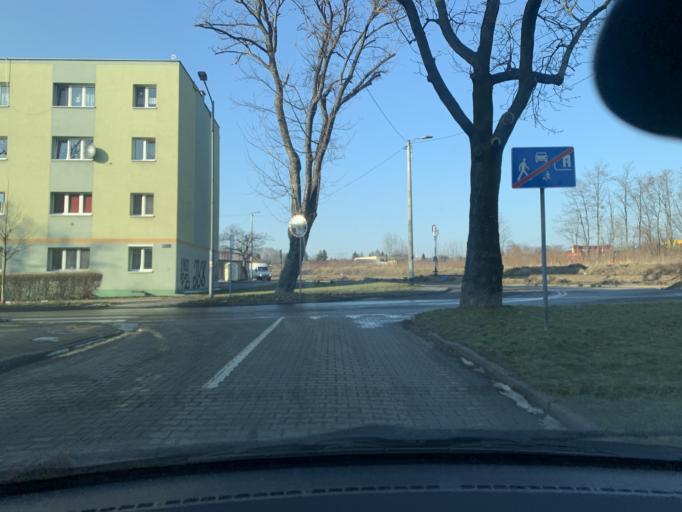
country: PL
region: Silesian Voivodeship
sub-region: Powiat tarnogorski
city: Radzionkow
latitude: 50.3854
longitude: 18.9052
